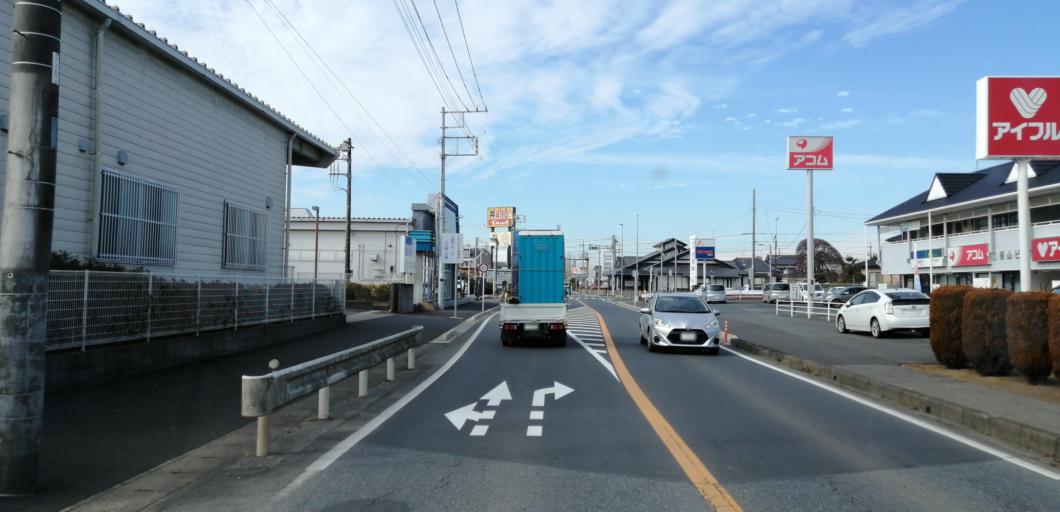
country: JP
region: Chiba
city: Narita
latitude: 35.7357
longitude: 140.3304
